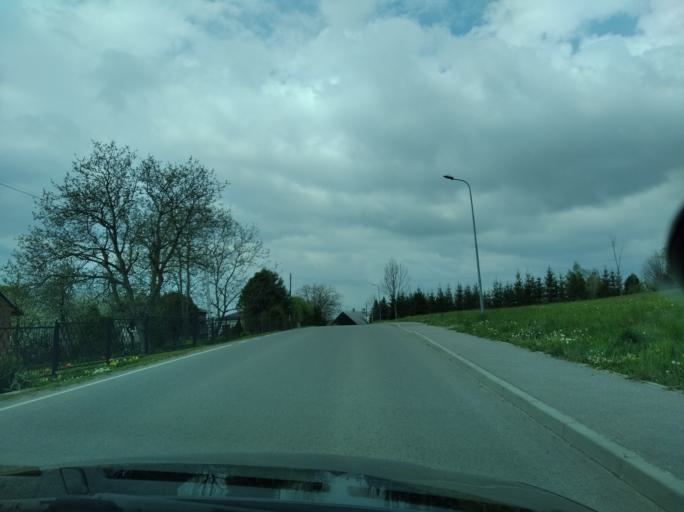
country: PL
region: Subcarpathian Voivodeship
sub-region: Powiat brzozowski
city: Haczow
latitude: 49.6657
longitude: 21.9000
